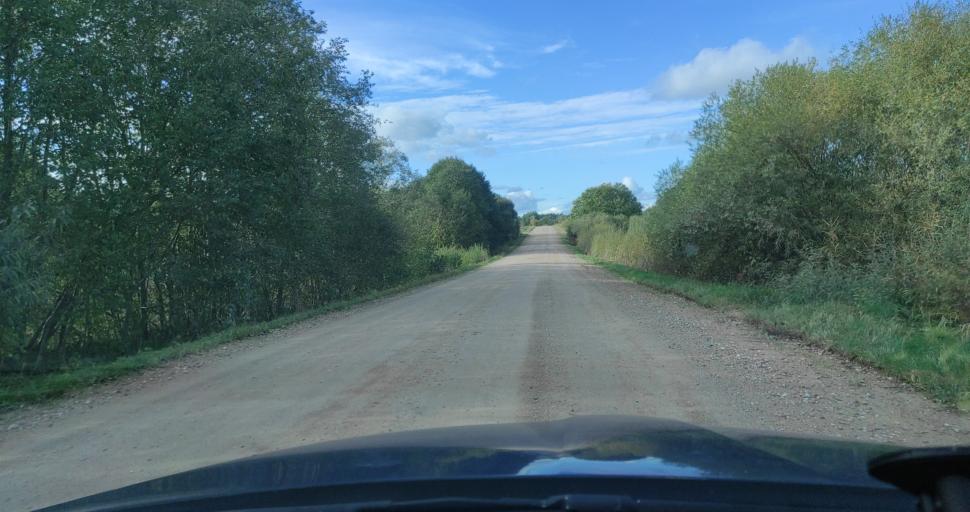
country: LV
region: Jaunpils
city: Jaunpils
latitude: 56.8301
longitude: 22.9930
